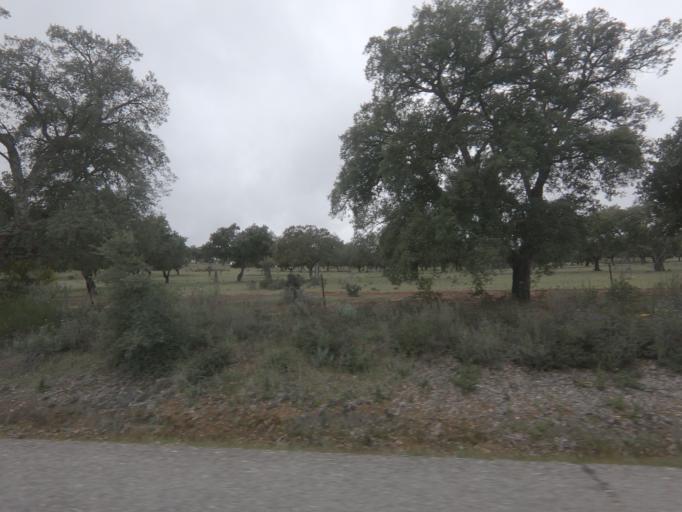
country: ES
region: Extremadura
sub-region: Provincia de Badajoz
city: Puebla de Obando
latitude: 39.2459
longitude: -6.5580
